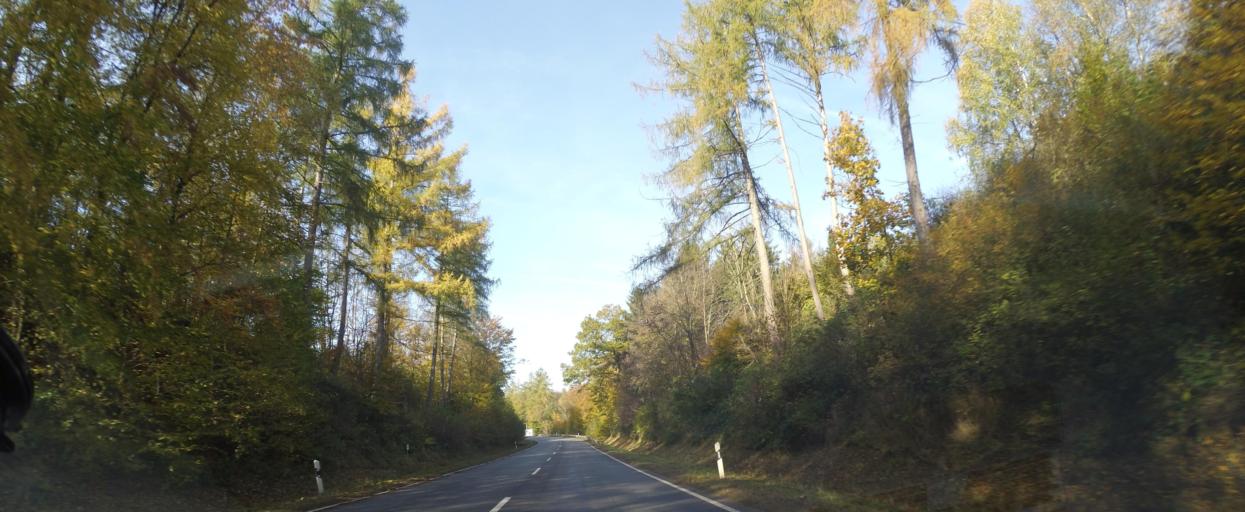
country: DE
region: Rheinland-Pfalz
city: Neuhutten
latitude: 49.6062
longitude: 7.0124
